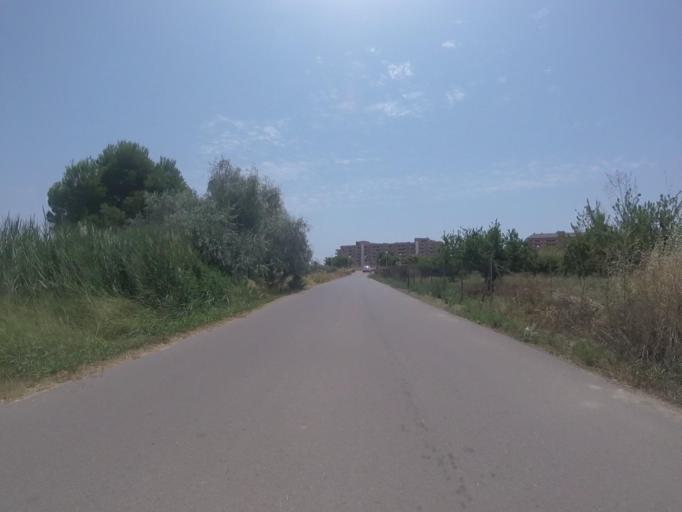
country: ES
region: Valencia
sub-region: Provincia de Castello
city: Orpesa/Oropesa del Mar
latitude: 40.1390
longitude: 0.1618
